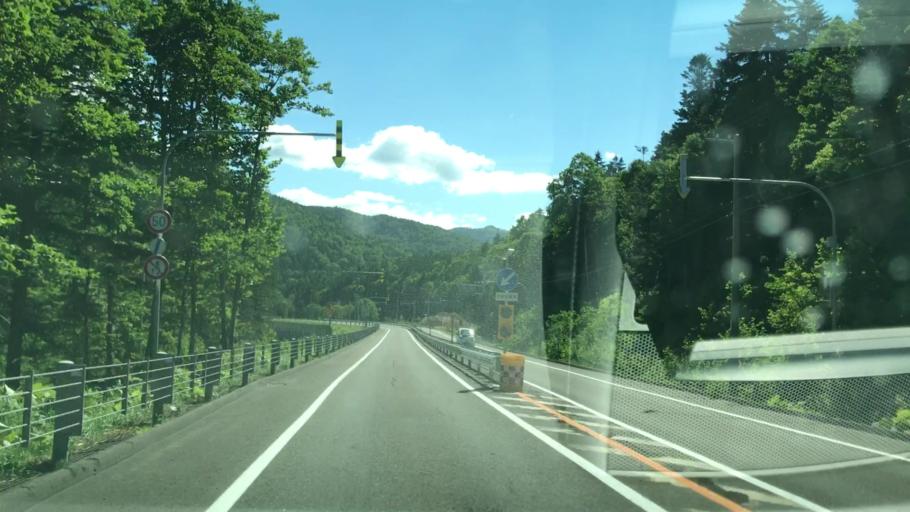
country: JP
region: Hokkaido
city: Shimo-furano
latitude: 42.9701
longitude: 142.6759
